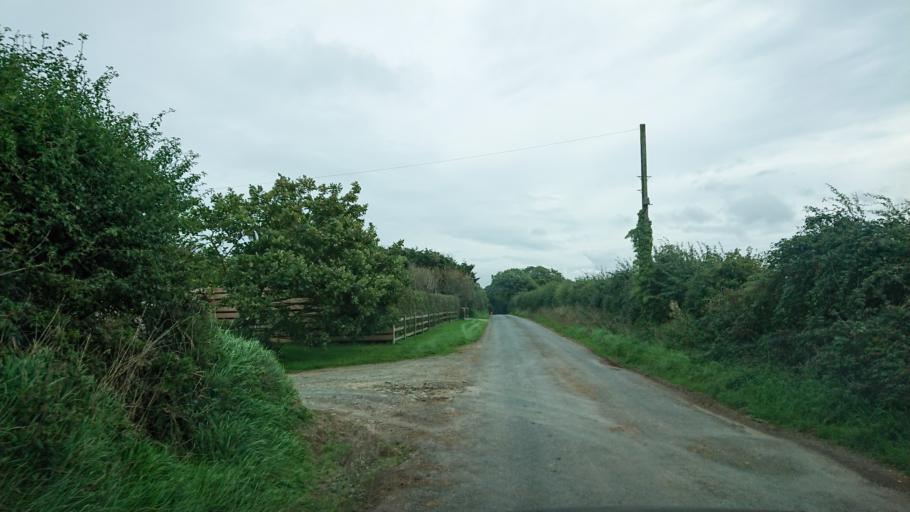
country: IE
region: Munster
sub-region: Waterford
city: Dunmore East
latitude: 52.1793
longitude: -6.9930
